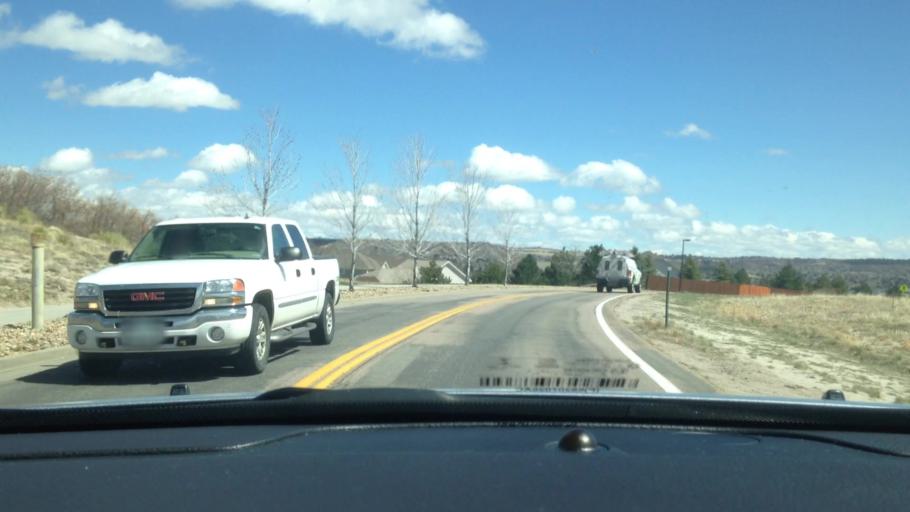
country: US
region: Colorado
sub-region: Douglas County
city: Castle Rock
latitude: 39.3746
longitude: -104.8801
